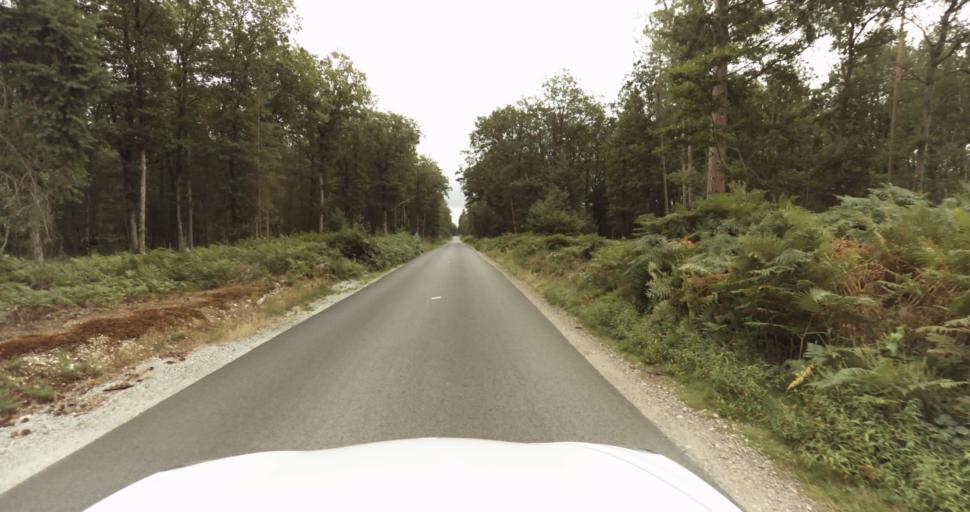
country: FR
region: Haute-Normandie
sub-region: Departement de l'Eure
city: Saint-Sebastien-de-Morsent
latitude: 48.9651
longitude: 1.0496
